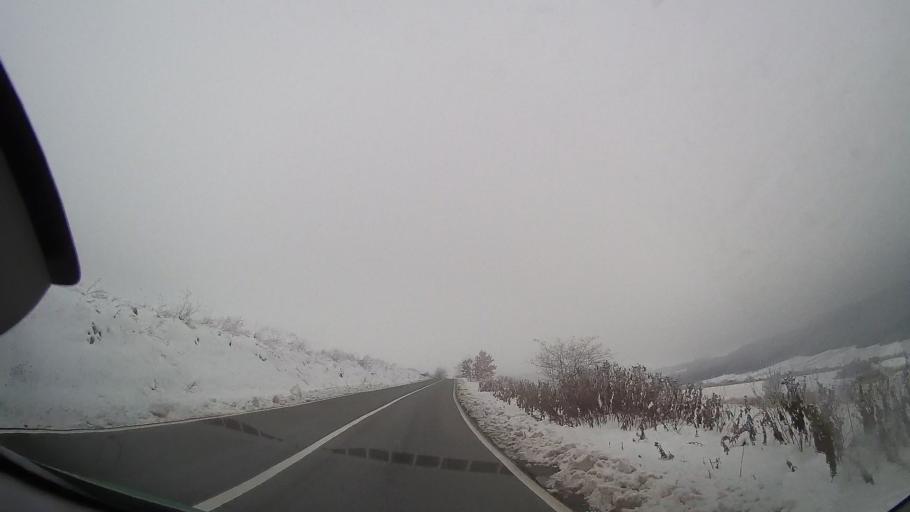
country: RO
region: Neamt
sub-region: Comuna Poenari
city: Poienari
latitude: 46.8725
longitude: 27.1410
